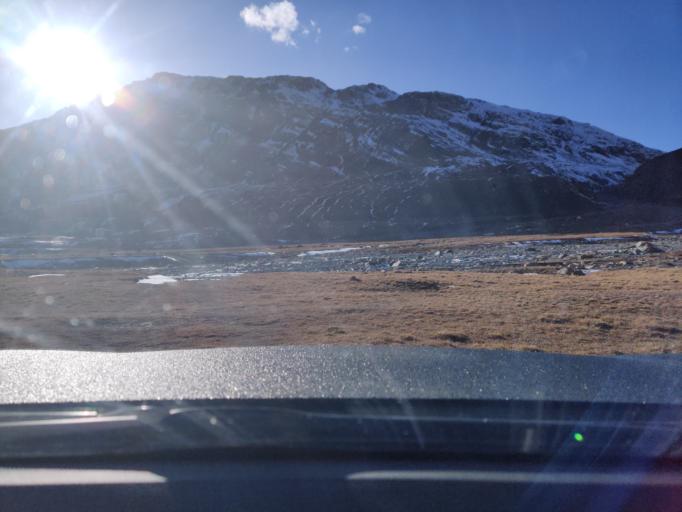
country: KG
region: Ysyk-Koel
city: Kadzhi-Say
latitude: 41.8123
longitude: 77.5783
